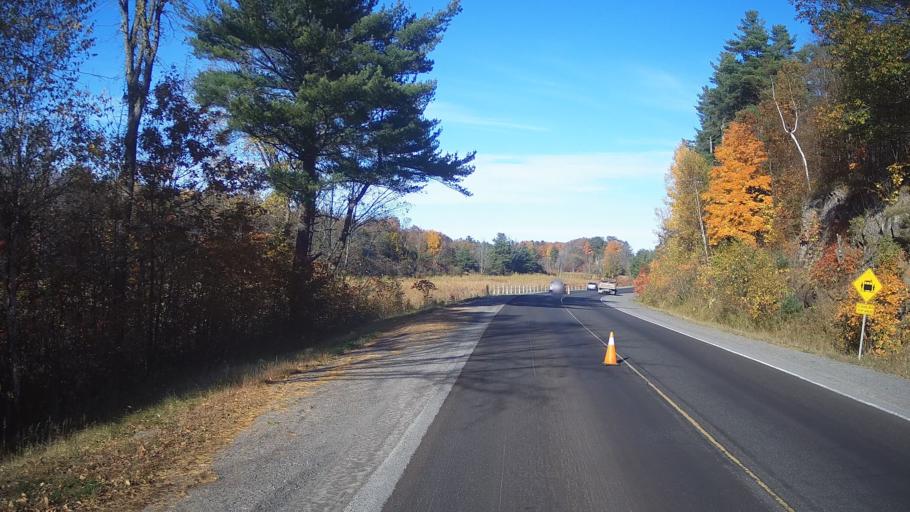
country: CA
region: Ontario
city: Kingston
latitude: 44.5195
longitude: -76.4601
